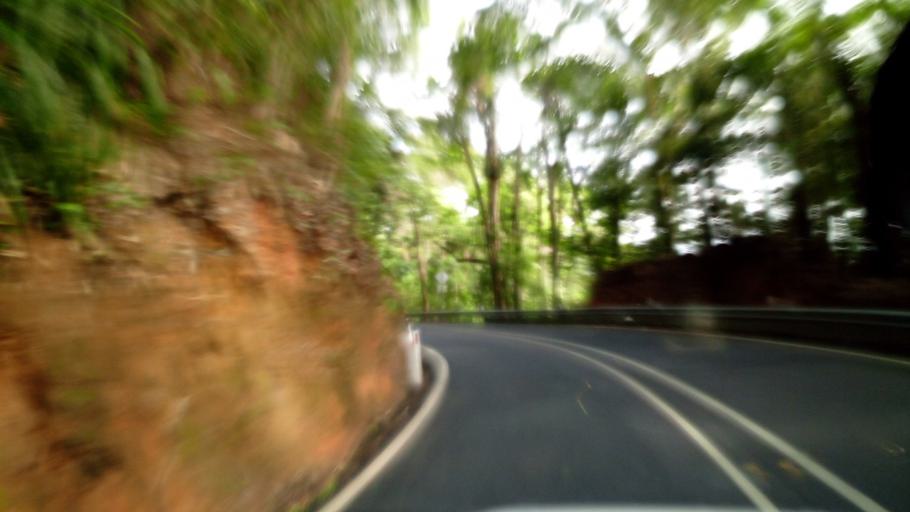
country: AU
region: Queensland
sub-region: Tablelands
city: Kuranda
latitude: -16.8416
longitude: 145.6716
